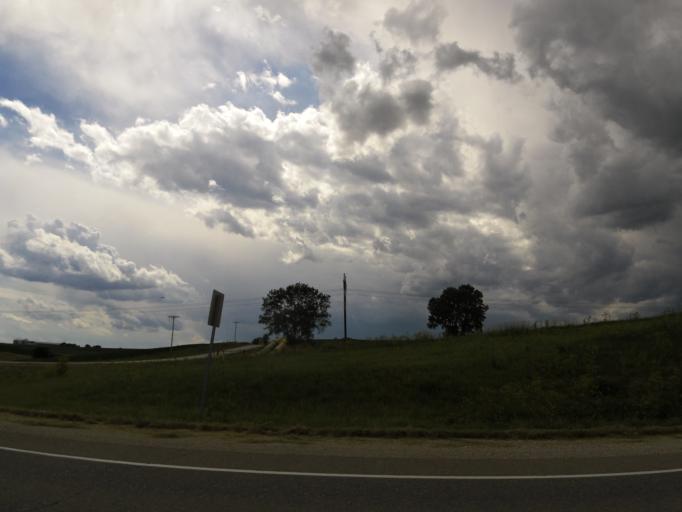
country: US
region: Iowa
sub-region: Washington County
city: Washington
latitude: 41.3774
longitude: -91.5511
